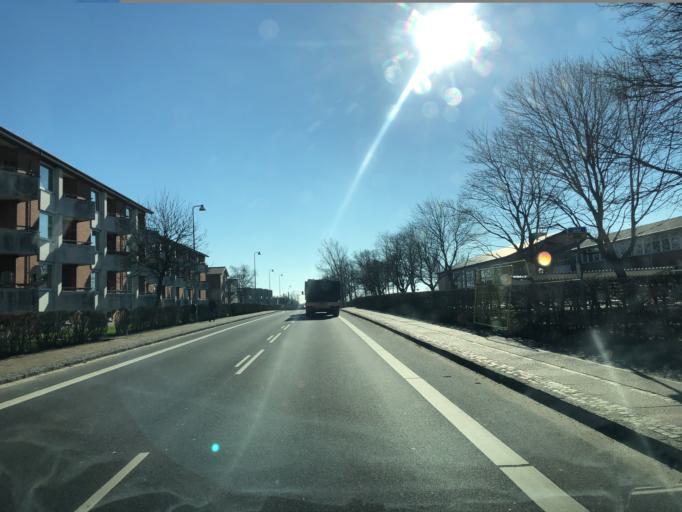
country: DK
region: Central Jutland
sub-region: Ikast-Brande Kommune
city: Ikast
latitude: 56.1388
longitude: 9.1645
